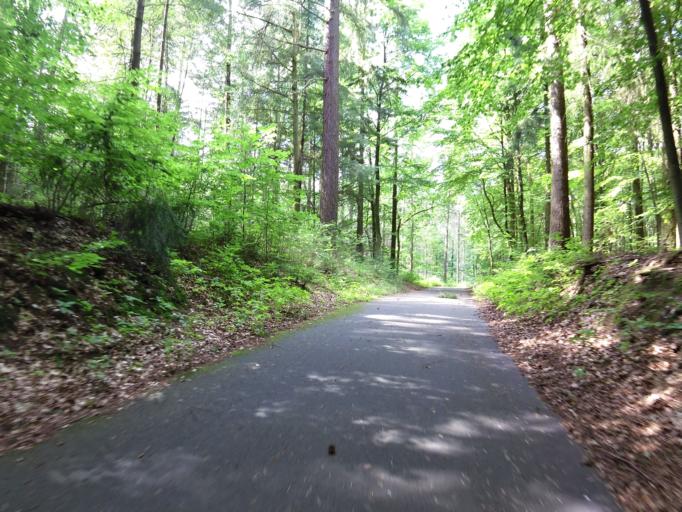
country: DE
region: Brandenburg
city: Lychen
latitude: 53.1883
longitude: 13.3422
